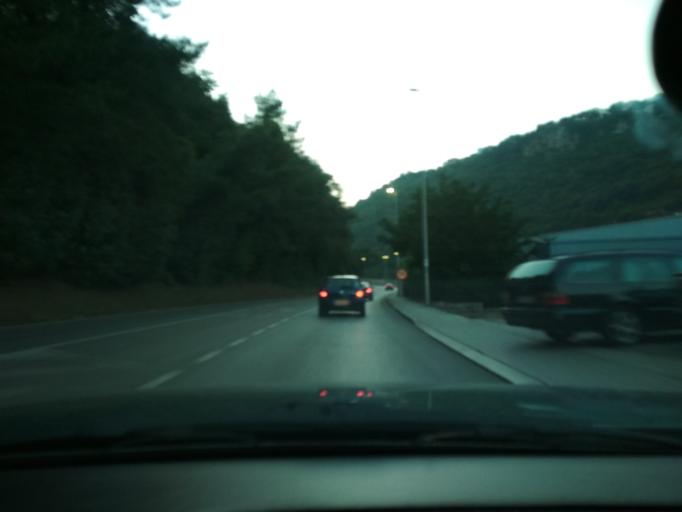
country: ME
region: Herceg Novi
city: Herceg-Novi
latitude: 42.4549
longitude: 18.5542
